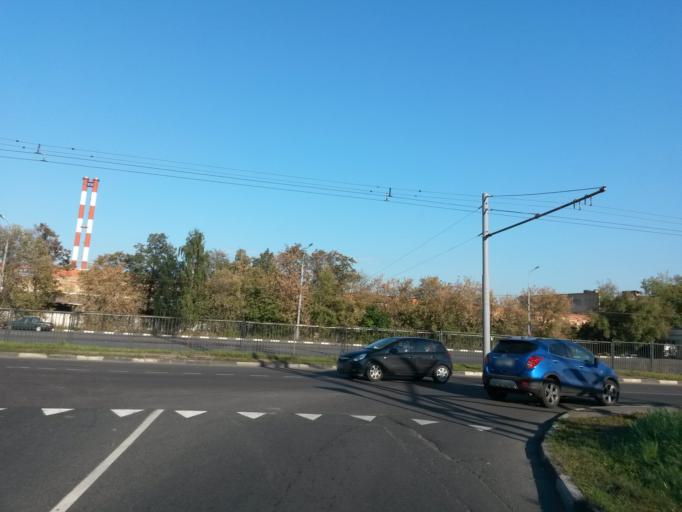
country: RU
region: Moskovskaya
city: Kur'yanovo
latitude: 55.6438
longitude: 37.7070
